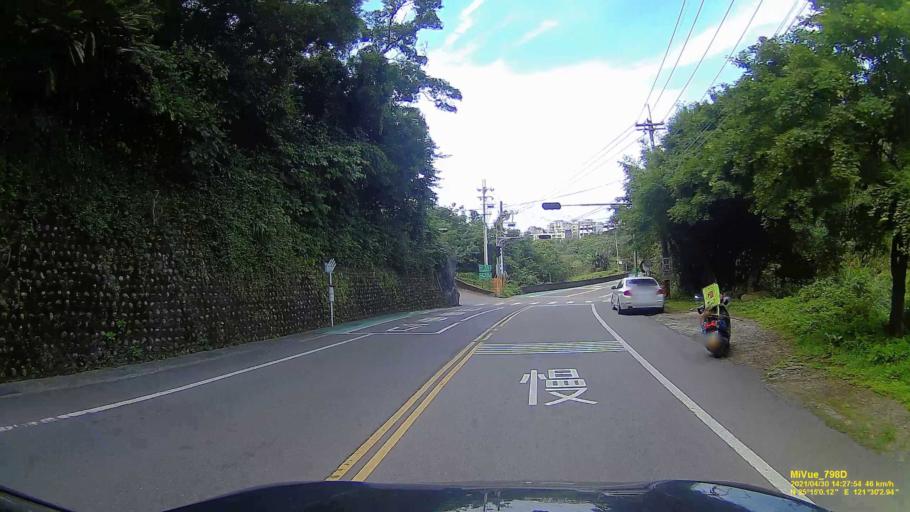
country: TW
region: Taipei
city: Taipei
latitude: 25.2504
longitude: 121.5010
